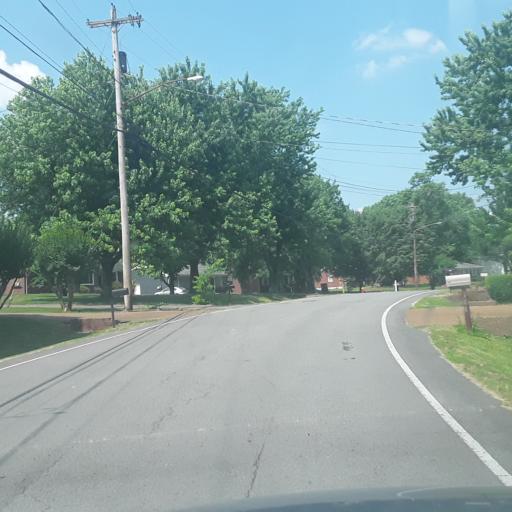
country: US
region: Tennessee
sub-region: Williamson County
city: Brentwood Estates
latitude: 36.0529
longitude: -86.7112
